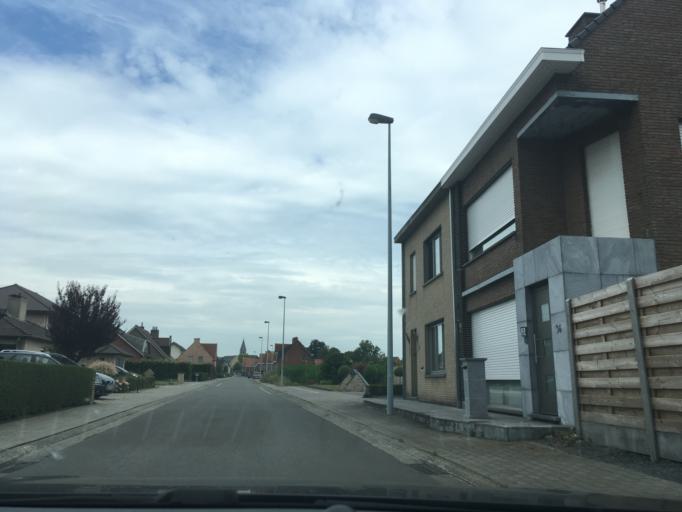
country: BE
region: Flanders
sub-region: Provincie West-Vlaanderen
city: Pittem
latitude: 50.9901
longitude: 3.2741
